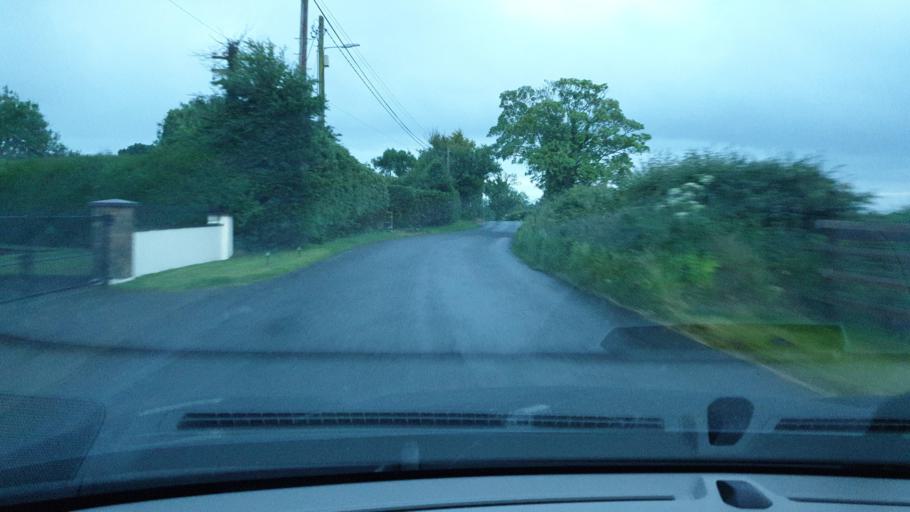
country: IE
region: Leinster
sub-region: An Mhi
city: Ashbourne
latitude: 53.5301
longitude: -6.3396
